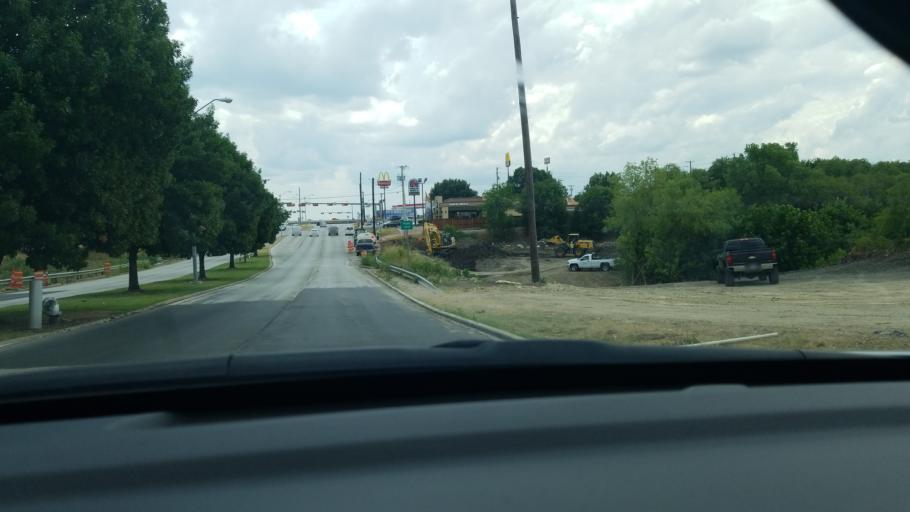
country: US
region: Texas
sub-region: Dallas County
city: Grand Prairie
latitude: 32.6805
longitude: -97.0444
